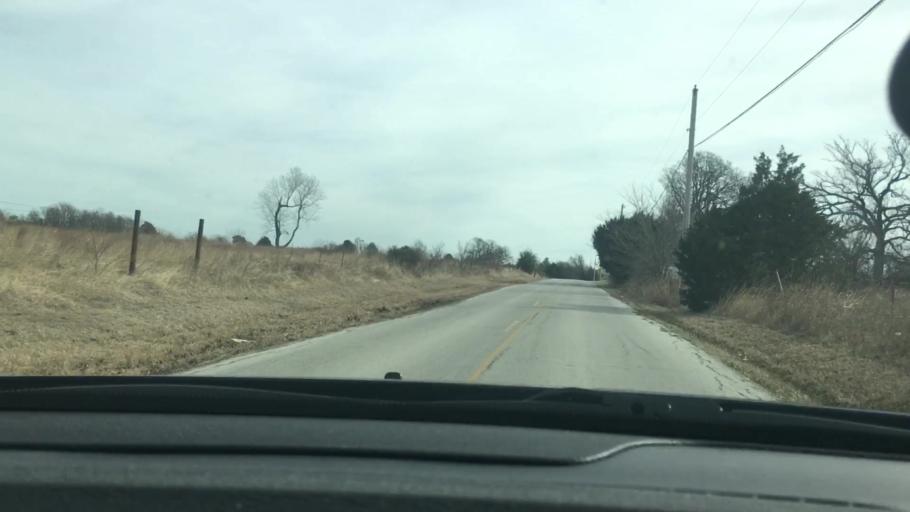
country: US
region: Oklahoma
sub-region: Carter County
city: Ardmore
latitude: 34.1740
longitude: -97.0822
